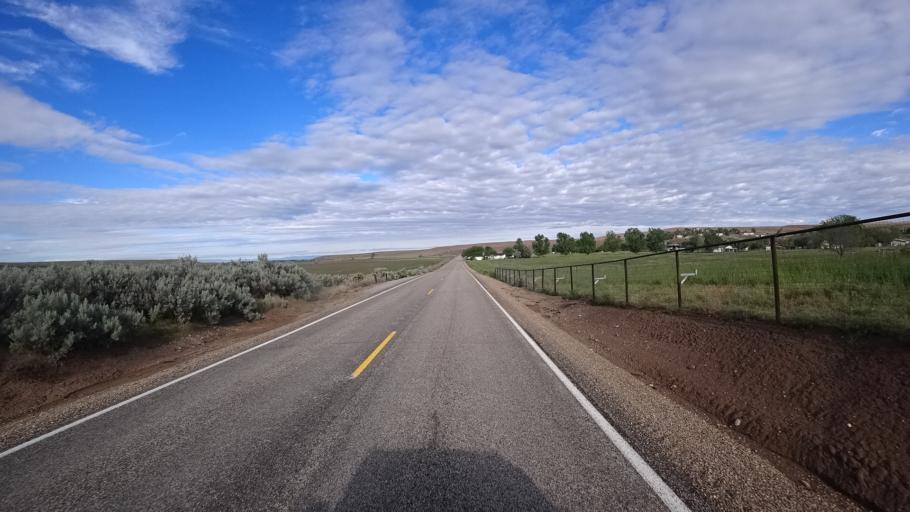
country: US
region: Idaho
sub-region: Ada County
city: Star
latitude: 43.7718
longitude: -116.4824
